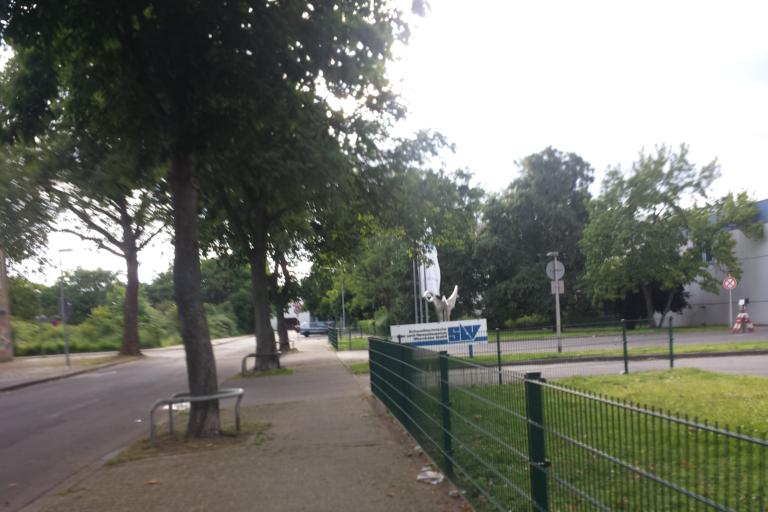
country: DE
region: Baden-Wuerttemberg
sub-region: Karlsruhe Region
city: Mannheim
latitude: 49.5059
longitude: 8.4740
